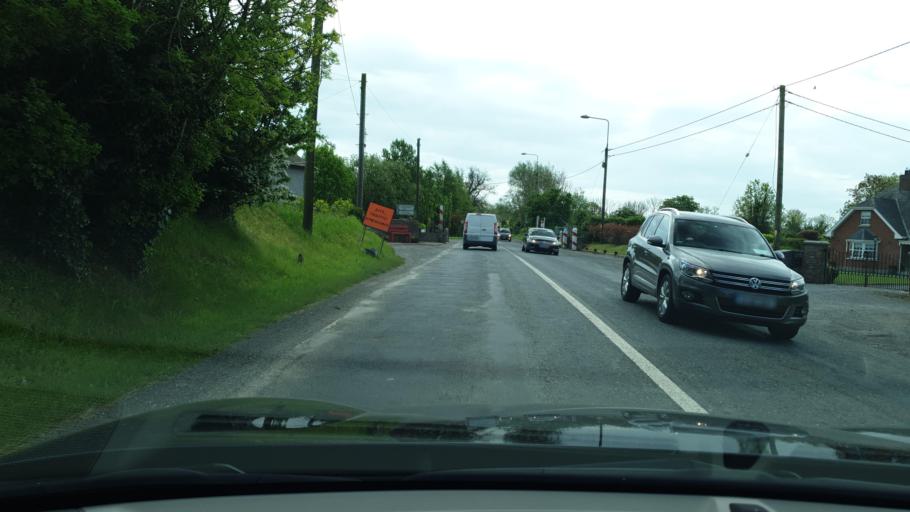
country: IE
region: Leinster
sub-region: An Mhi
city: Navan
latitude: 53.7346
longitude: -6.7114
